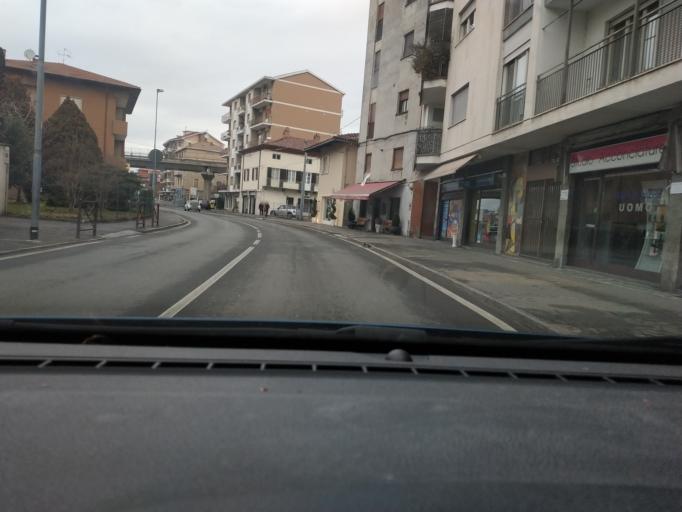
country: IT
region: Piedmont
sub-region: Provincia di Torino
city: Ivrea
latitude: 45.4562
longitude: 7.8792
